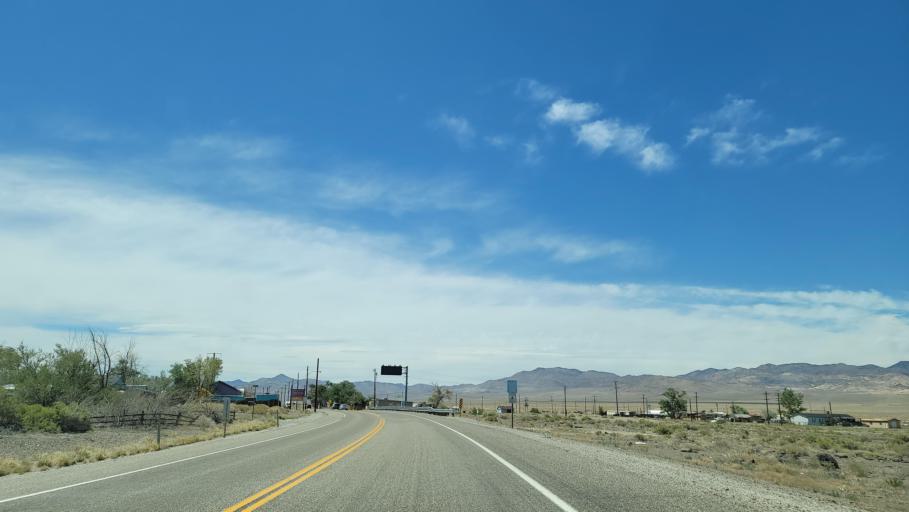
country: US
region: Nevada
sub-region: Mineral County
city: Hawthorne
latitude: 38.5035
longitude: -118.1759
